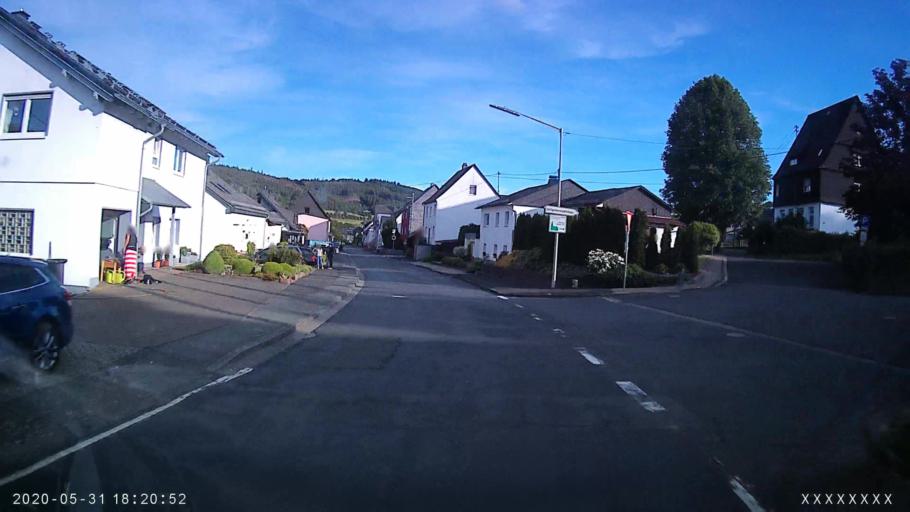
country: DE
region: Hesse
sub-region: Regierungsbezirk Giessen
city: Haiger
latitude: 50.7743
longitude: 8.2074
